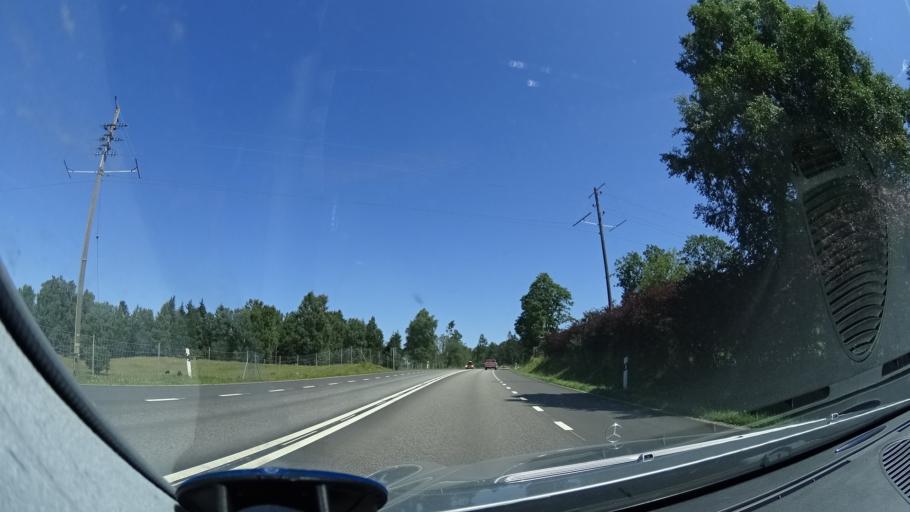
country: SE
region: Skane
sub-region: Horby Kommun
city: Hoerby
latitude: 55.9270
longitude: 13.7971
